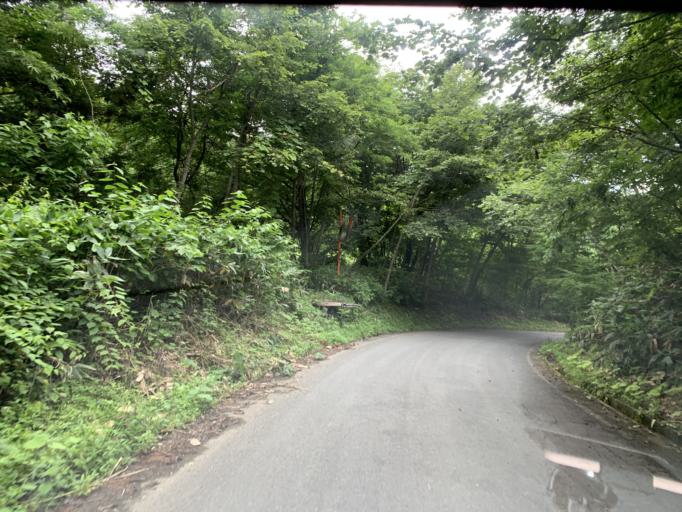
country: JP
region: Iwate
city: Ichinoseki
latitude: 38.9622
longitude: 140.8990
